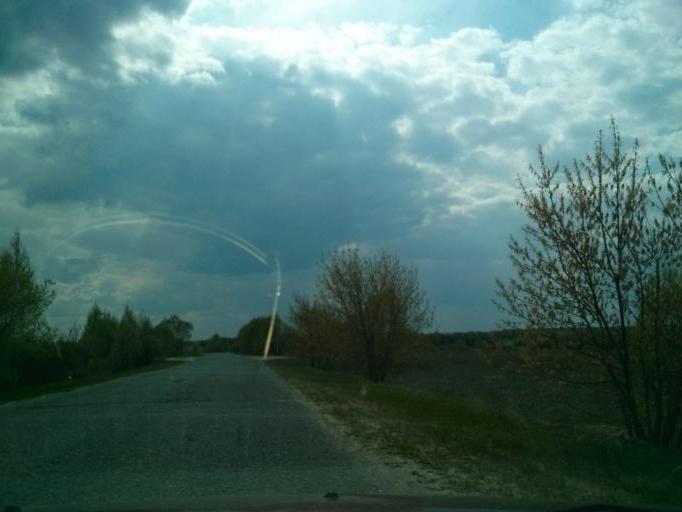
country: RU
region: Nizjnij Novgorod
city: Shimorskoye
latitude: 55.3804
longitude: 41.9366
